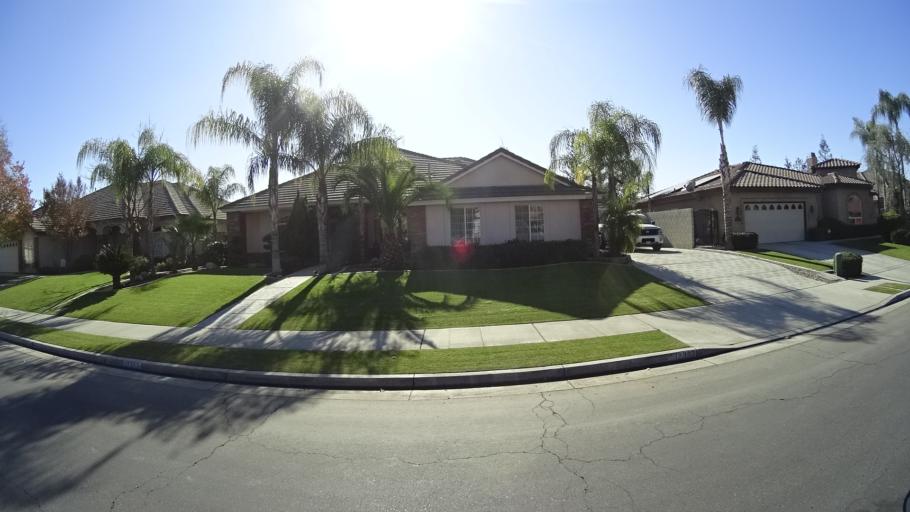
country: US
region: California
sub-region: Kern County
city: Rosedale
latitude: 35.3643
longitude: -119.1388
